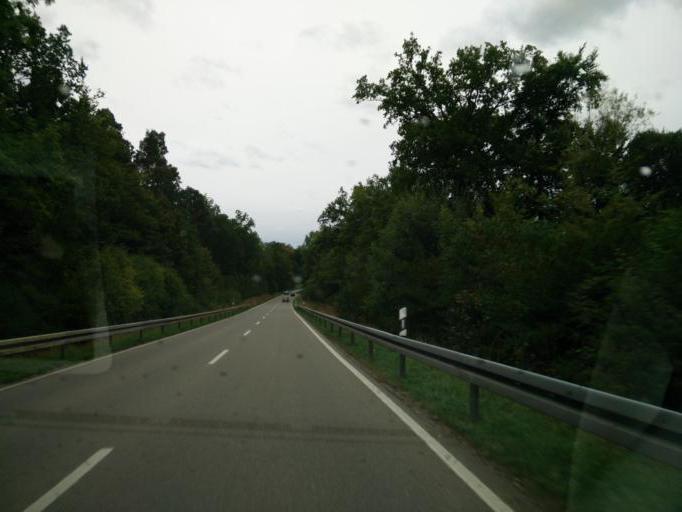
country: DE
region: Baden-Wuerttemberg
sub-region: Tuebingen Region
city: Dettenhausen
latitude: 48.5749
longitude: 9.1047
